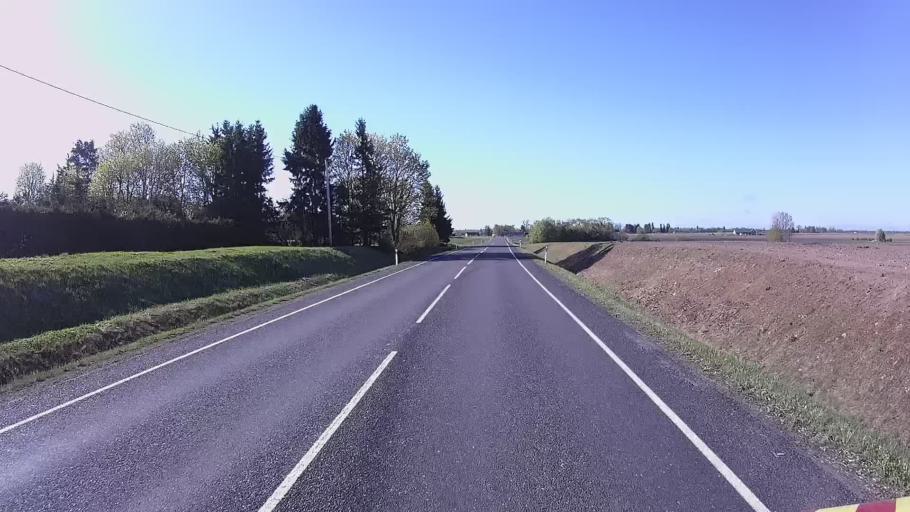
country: EE
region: Viljandimaa
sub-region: Vohma linn
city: Vohma
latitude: 58.6675
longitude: 25.6072
